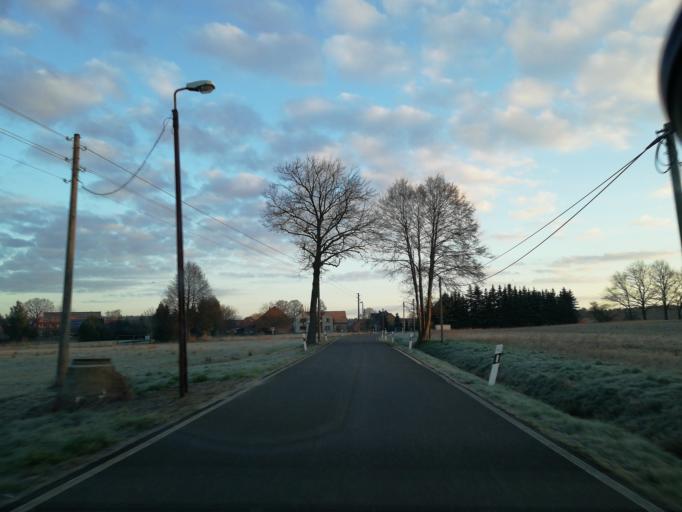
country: DE
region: Brandenburg
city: Crinitz
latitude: 51.7323
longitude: 13.8318
